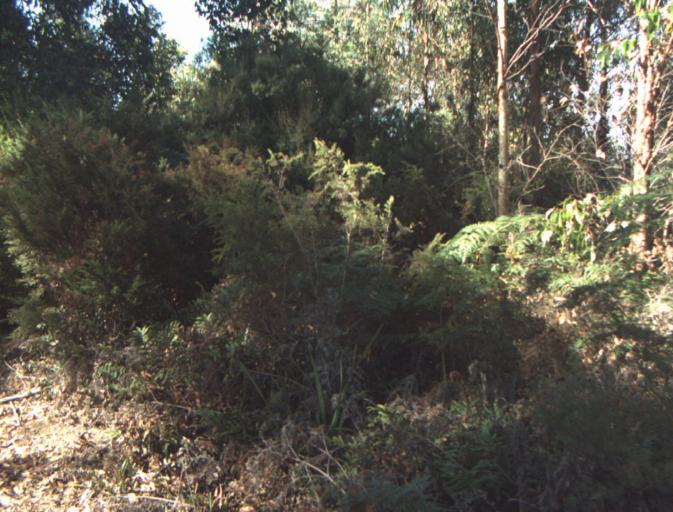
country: AU
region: Tasmania
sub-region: Dorset
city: Scottsdale
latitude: -41.2995
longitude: 147.3549
